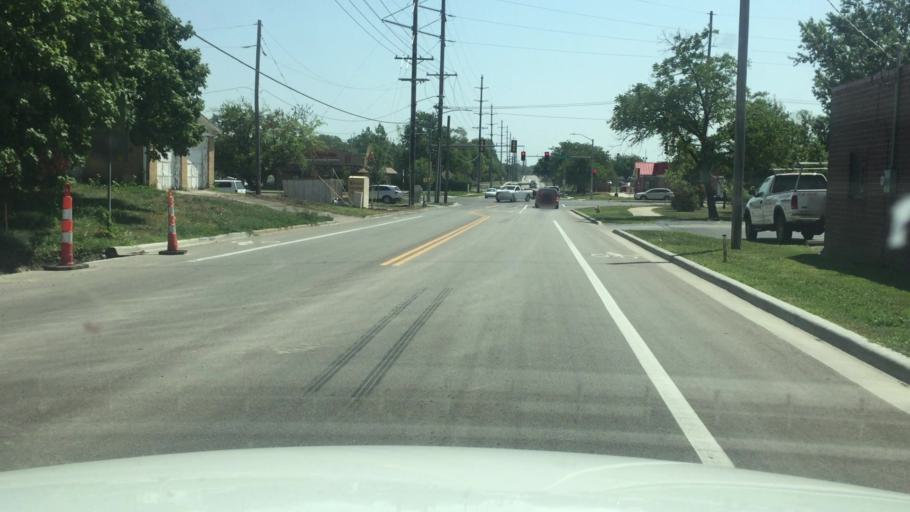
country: US
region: Kansas
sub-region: Johnson County
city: Olathe
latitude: 38.8691
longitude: -94.8171
